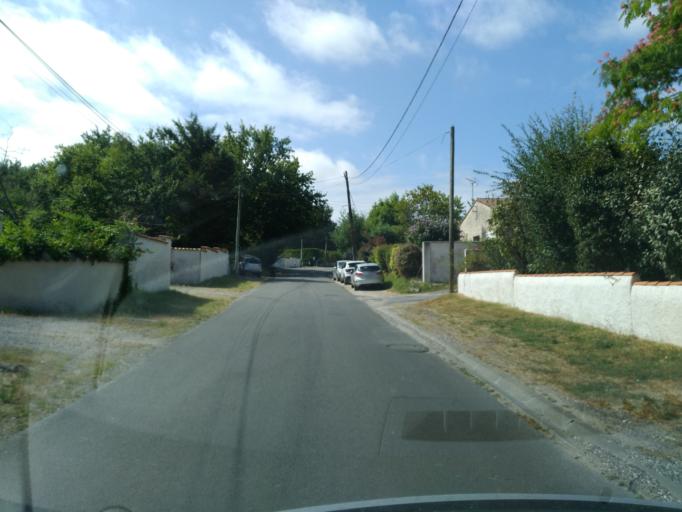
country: FR
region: Poitou-Charentes
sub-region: Departement de la Charente-Maritime
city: Breuillet
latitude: 45.6884
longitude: -1.0735
